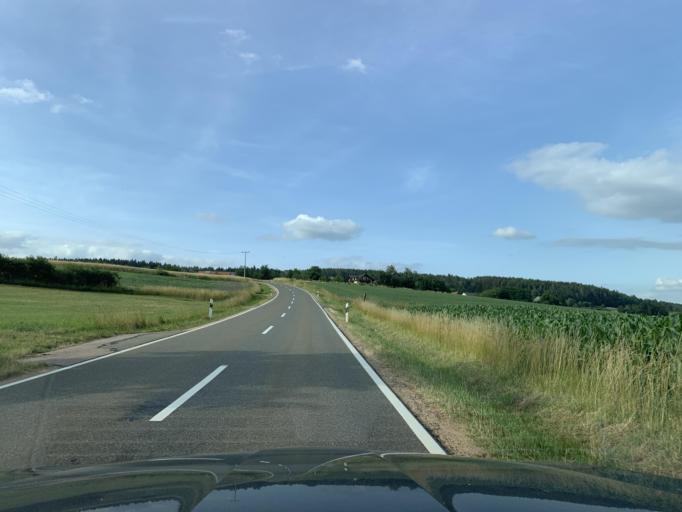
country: DE
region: Bavaria
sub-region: Upper Palatinate
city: Bach
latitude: 49.4051
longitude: 12.3606
